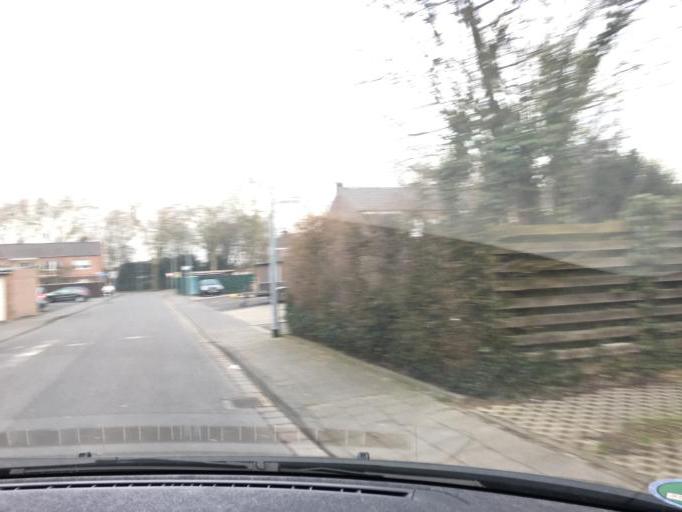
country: DE
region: North Rhine-Westphalia
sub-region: Regierungsbezirk Dusseldorf
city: Monchengladbach
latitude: 51.1377
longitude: 6.4095
